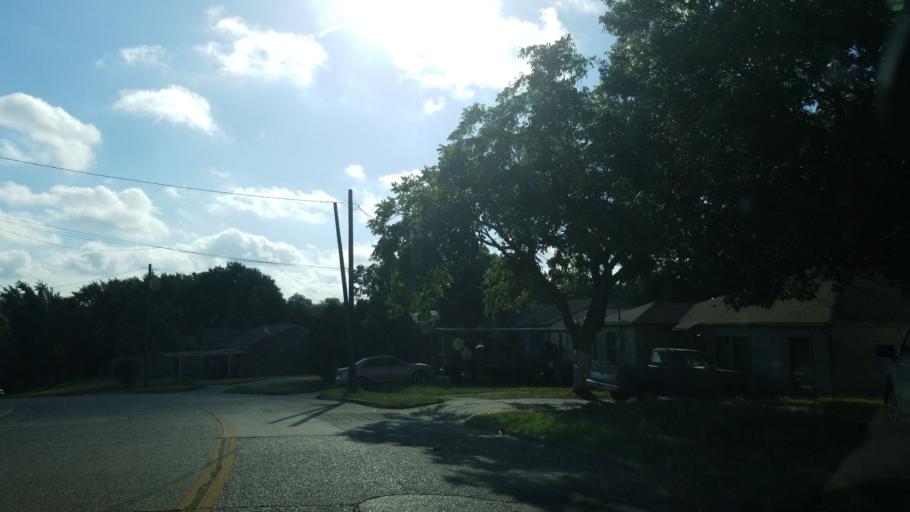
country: US
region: Texas
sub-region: Dallas County
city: Dallas
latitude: 32.7318
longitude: -96.8020
